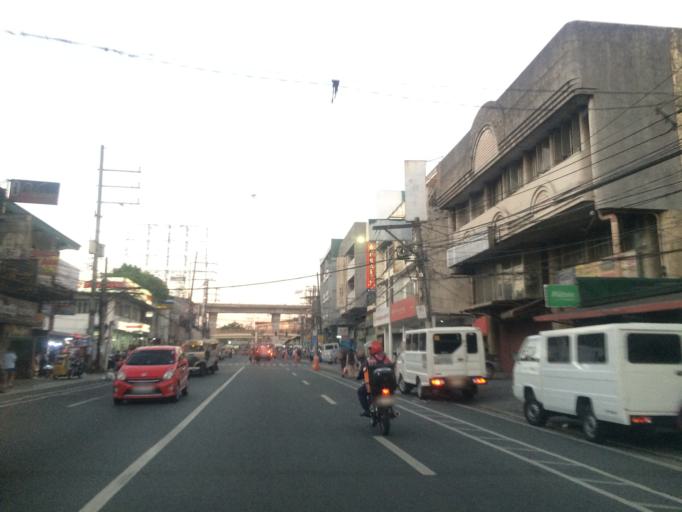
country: PH
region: Calabarzon
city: Del Monte
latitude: 14.6559
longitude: 121.0190
